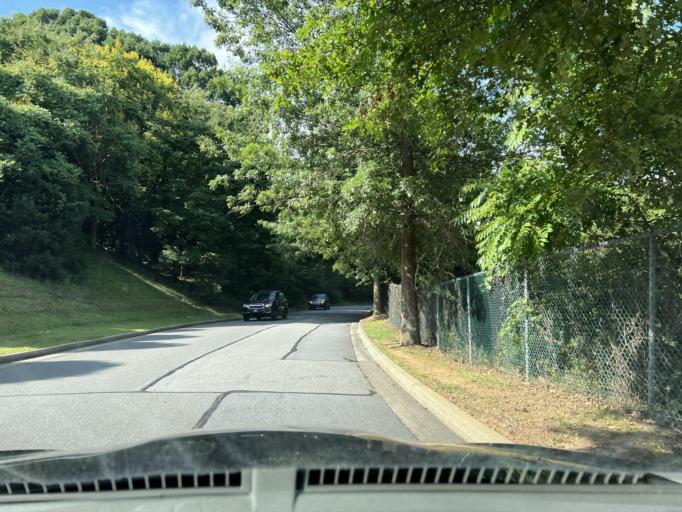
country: US
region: North Carolina
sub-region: Buncombe County
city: Biltmore Forest
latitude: 35.5736
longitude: -82.5236
